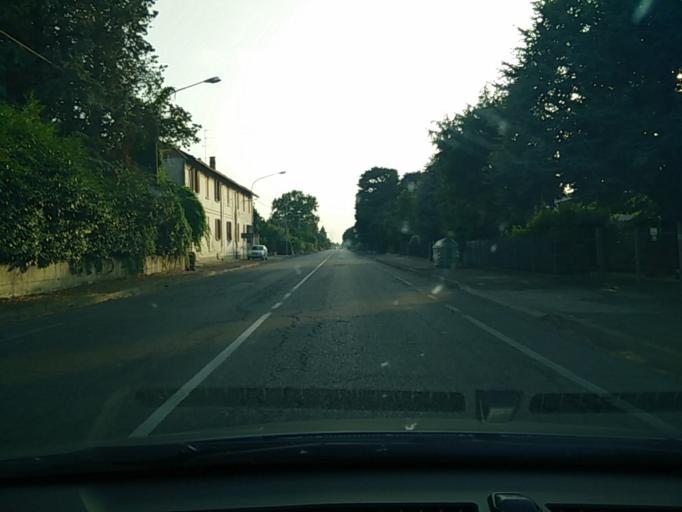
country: IT
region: Lombardy
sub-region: Provincia di Pavia
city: Redavalle
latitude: 45.0388
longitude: 9.2018
